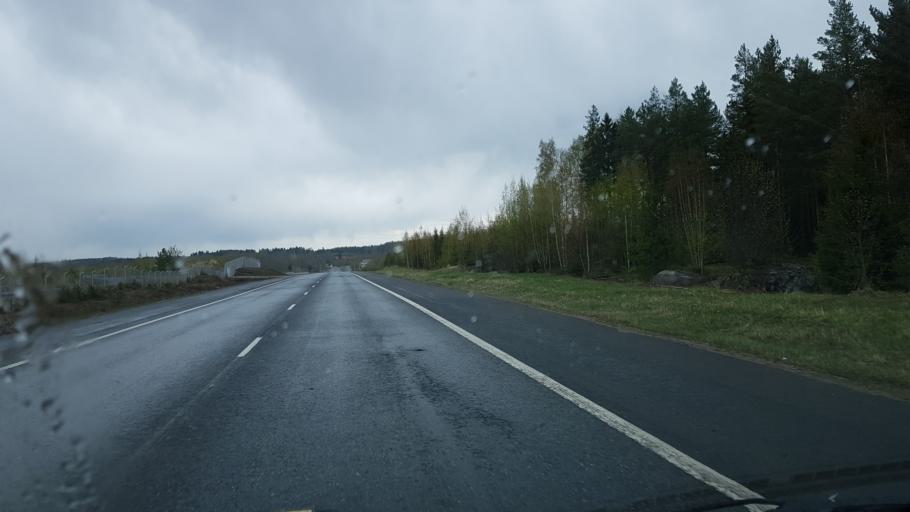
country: FI
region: Pirkanmaa
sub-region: Tampere
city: Pirkkala
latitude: 61.4158
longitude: 23.6343
